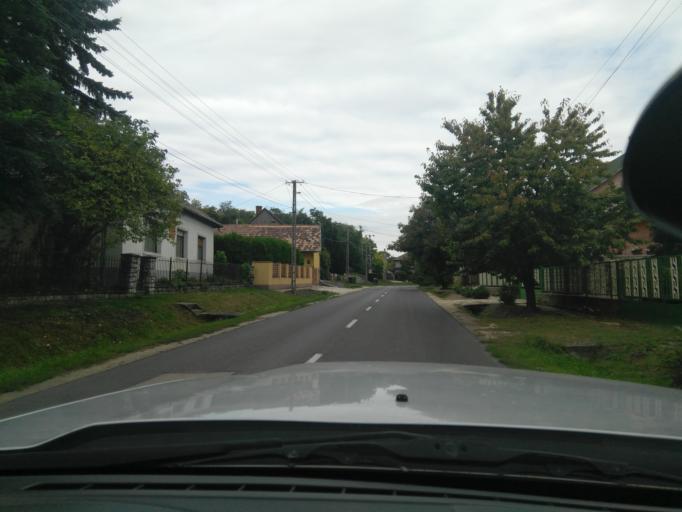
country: HU
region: Fejer
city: Val
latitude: 47.3649
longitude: 18.7358
